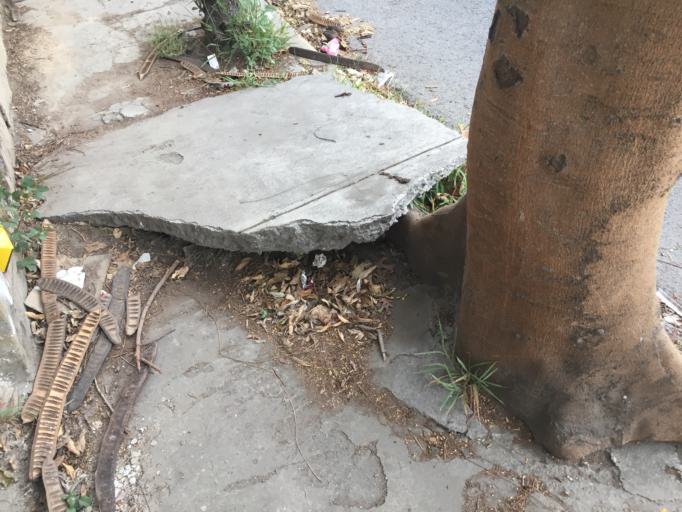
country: MX
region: Nuevo Leon
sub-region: Monterrey
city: Monterrey
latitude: 25.6789
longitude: -100.3071
